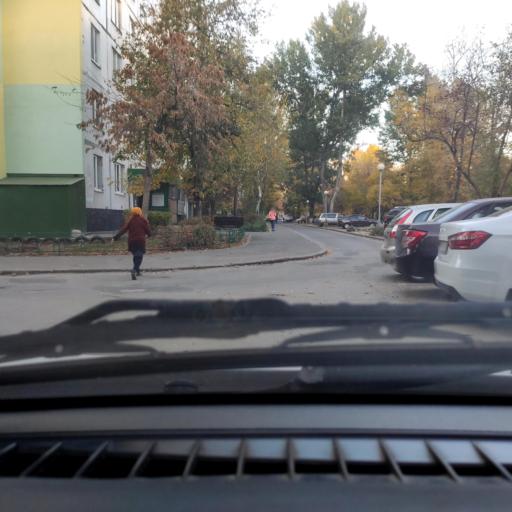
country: RU
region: Samara
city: Tol'yatti
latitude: 53.5099
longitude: 49.2793
